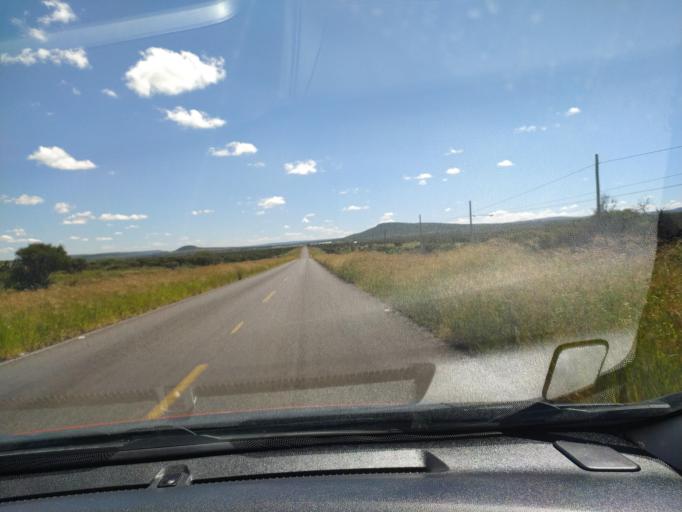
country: MX
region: Jalisco
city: San Miguel el Alto
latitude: 21.0177
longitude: -102.5039
